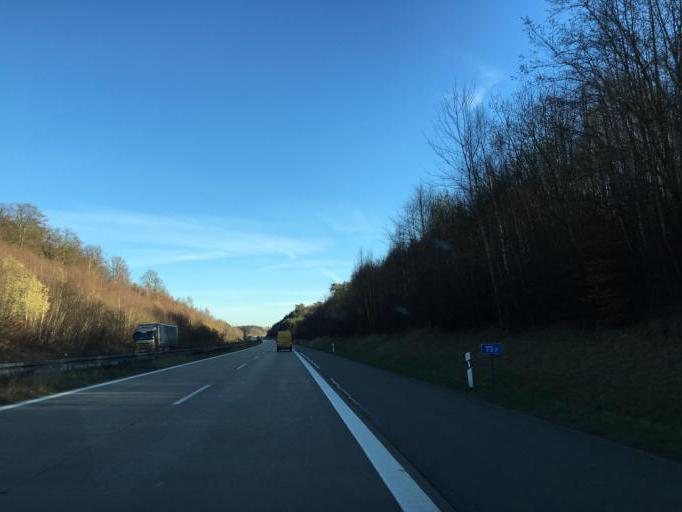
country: DE
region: Mecklenburg-Vorpommern
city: Lalendorf
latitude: 53.7390
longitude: 12.3390
